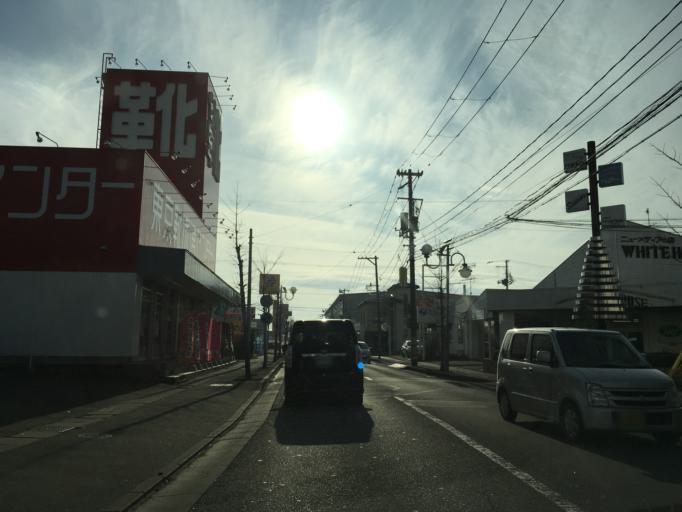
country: JP
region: Miyagi
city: Wakuya
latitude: 38.6896
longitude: 141.1895
